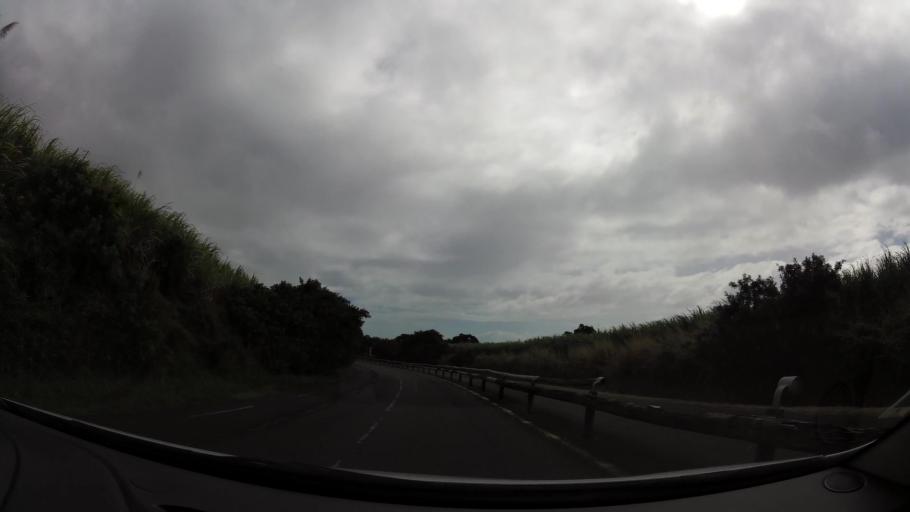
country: RE
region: Reunion
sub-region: Reunion
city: Sainte-Marie
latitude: -20.8940
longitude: 55.5563
